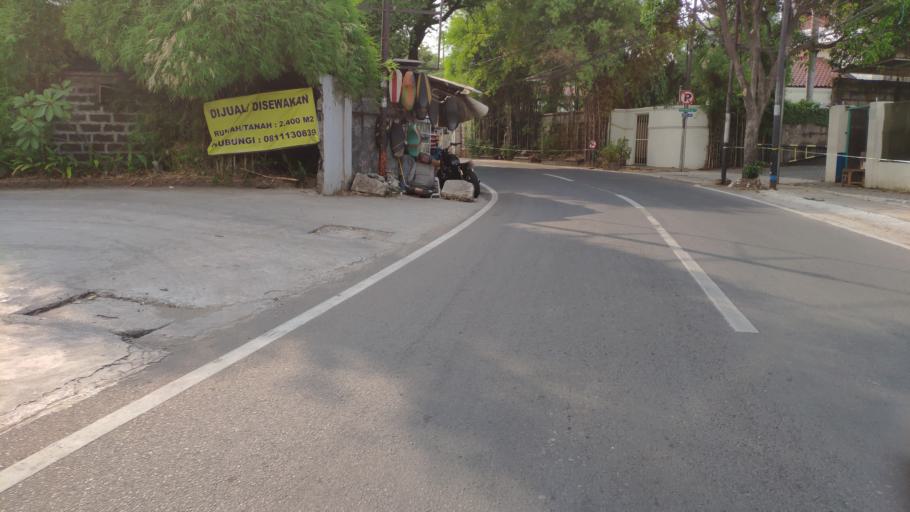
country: ID
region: West Java
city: Pamulang
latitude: -6.3162
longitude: 106.8144
